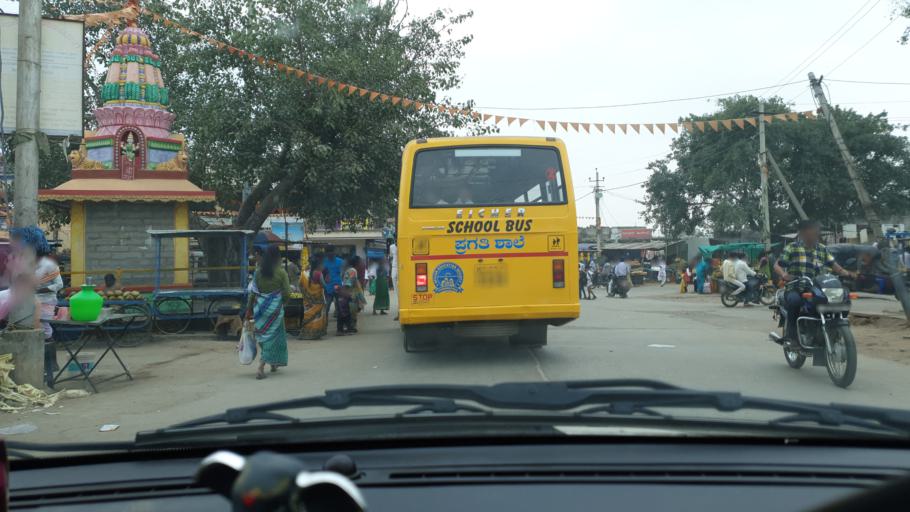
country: IN
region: Karnataka
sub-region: Yadgir
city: Gurmatkal
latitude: 16.8713
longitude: 77.3912
